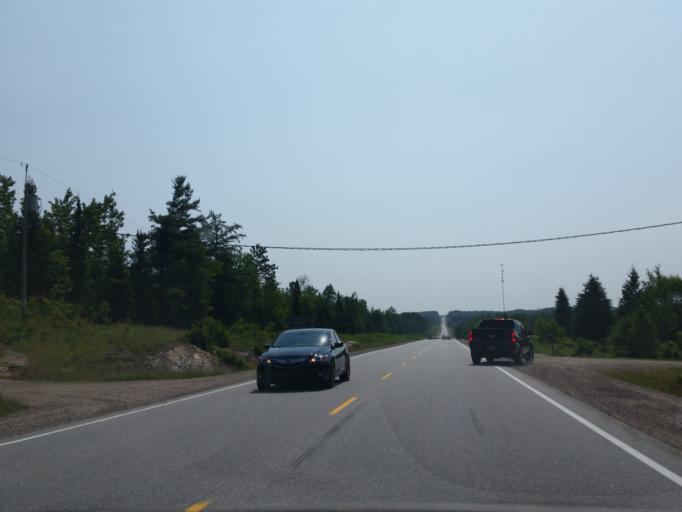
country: CA
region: Ontario
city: Mattawa
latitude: 46.2943
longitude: -78.5403
